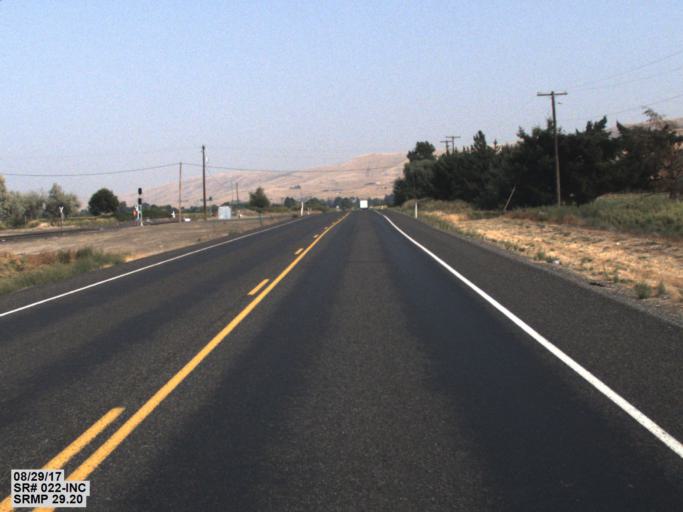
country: US
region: Washington
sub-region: Yakima County
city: Grandview
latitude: 46.1878
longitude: -119.8788
